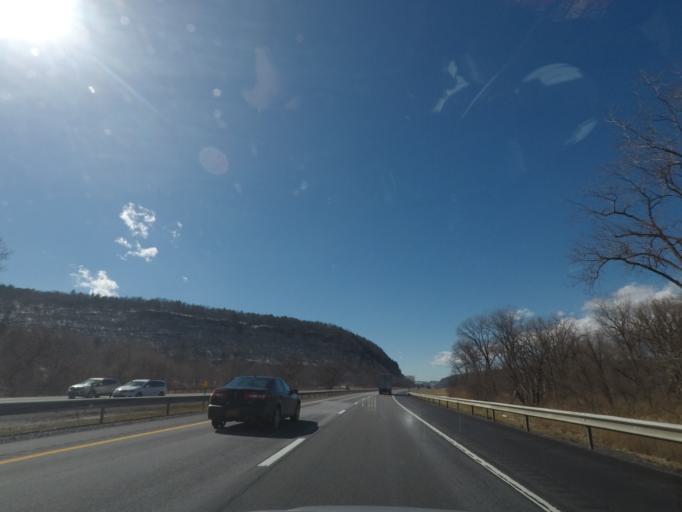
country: US
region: New York
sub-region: Montgomery County
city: Canajoharie
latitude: 42.8959
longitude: -74.4718
